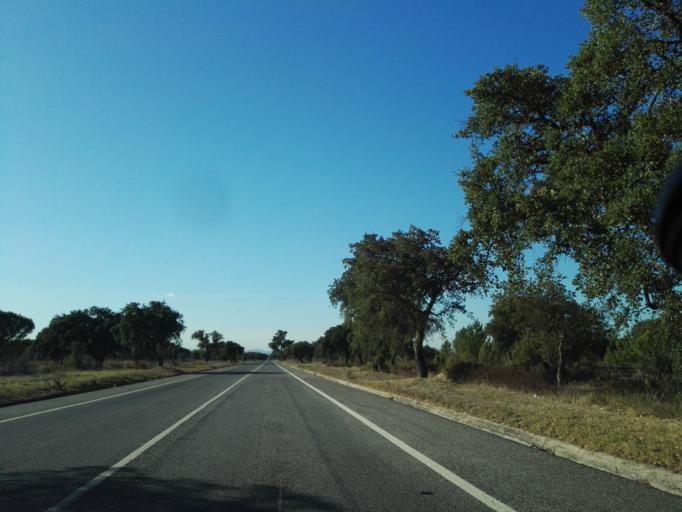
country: PT
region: Santarem
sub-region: Benavente
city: Poceirao
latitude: 38.8866
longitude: -8.8234
